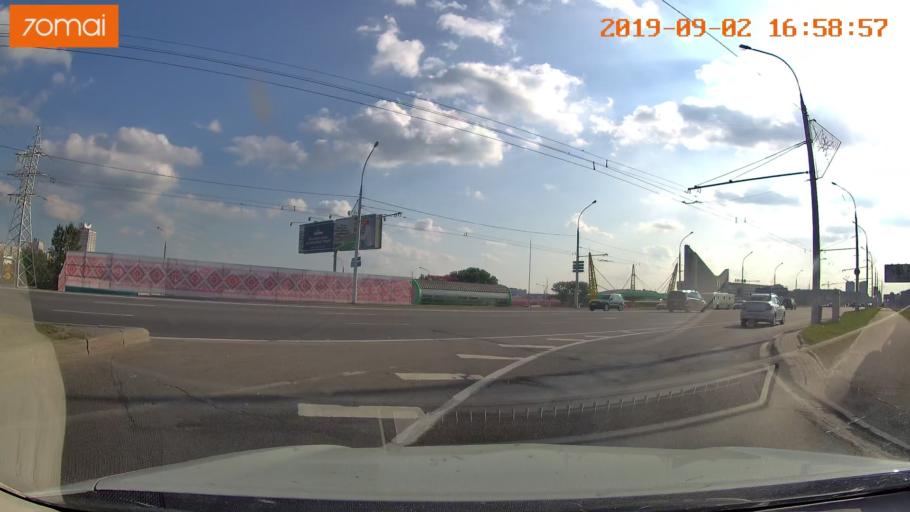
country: BY
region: Minsk
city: Borovlyany
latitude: 53.9427
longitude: 27.6755
